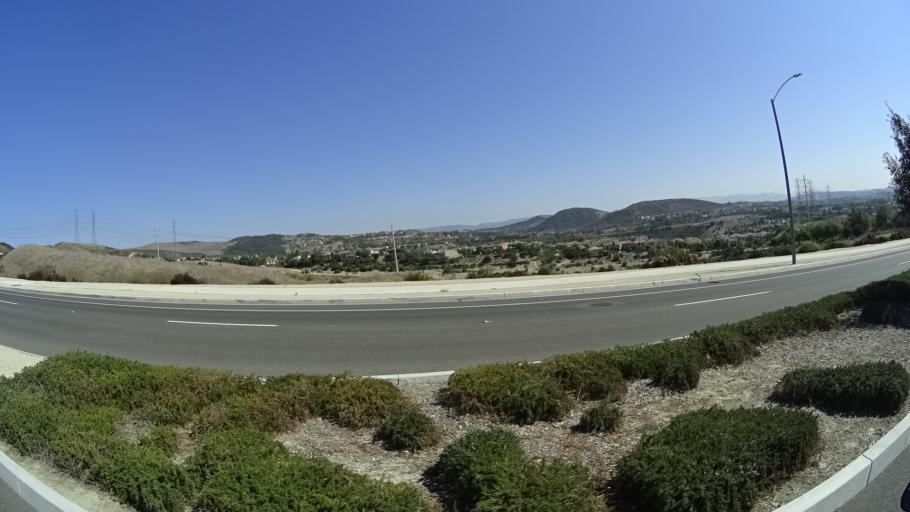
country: US
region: California
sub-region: Orange County
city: San Clemente
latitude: 33.4709
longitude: -117.6114
